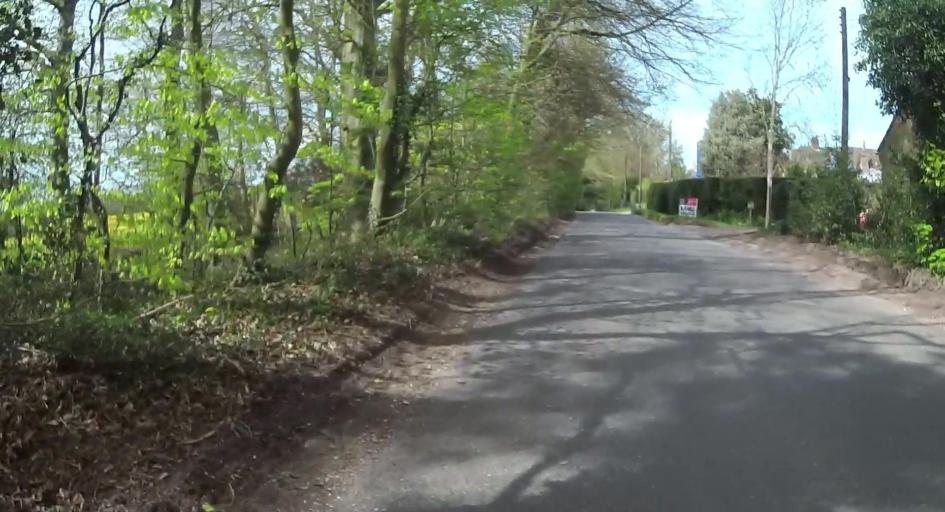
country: GB
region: England
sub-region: Hampshire
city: Winchester
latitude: 51.0592
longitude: -1.3569
